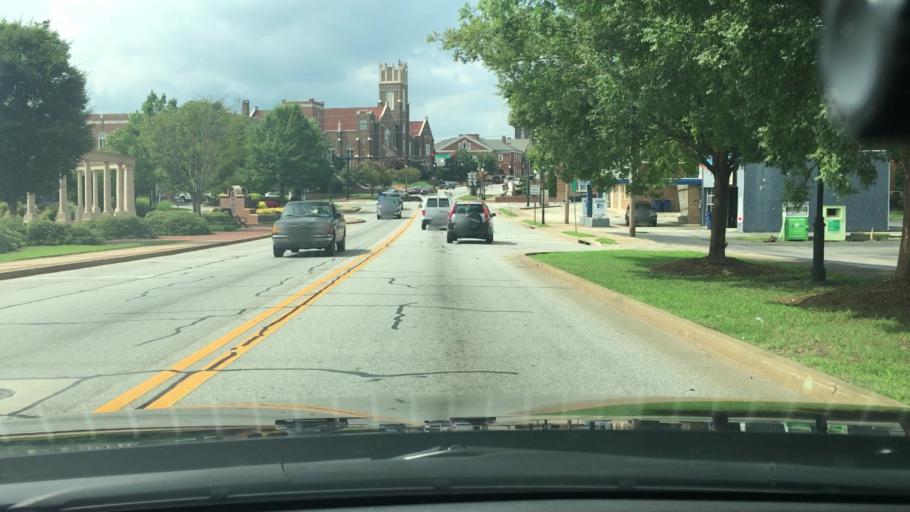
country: US
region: Georgia
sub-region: Coweta County
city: Newnan
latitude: 33.3711
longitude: -84.7995
